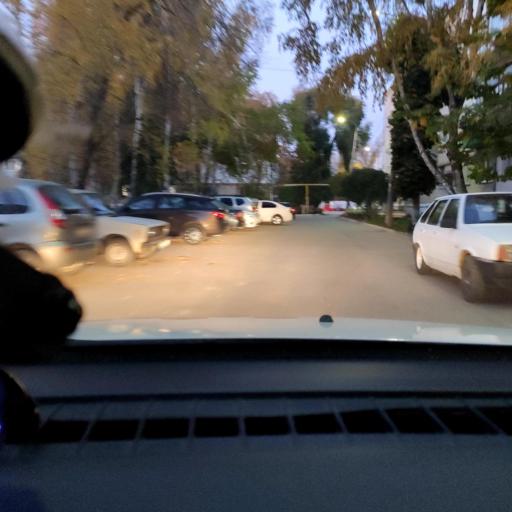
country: RU
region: Samara
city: Chapayevsk
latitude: 52.9958
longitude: 49.7771
